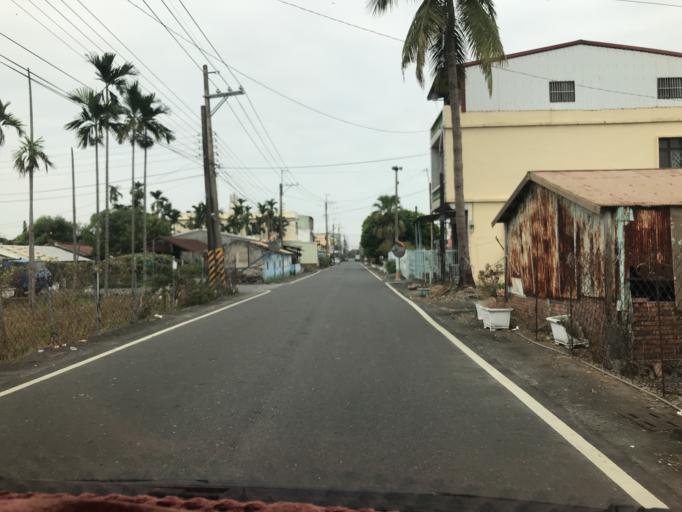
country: TW
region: Taiwan
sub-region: Pingtung
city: Pingtung
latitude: 22.5045
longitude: 120.5878
